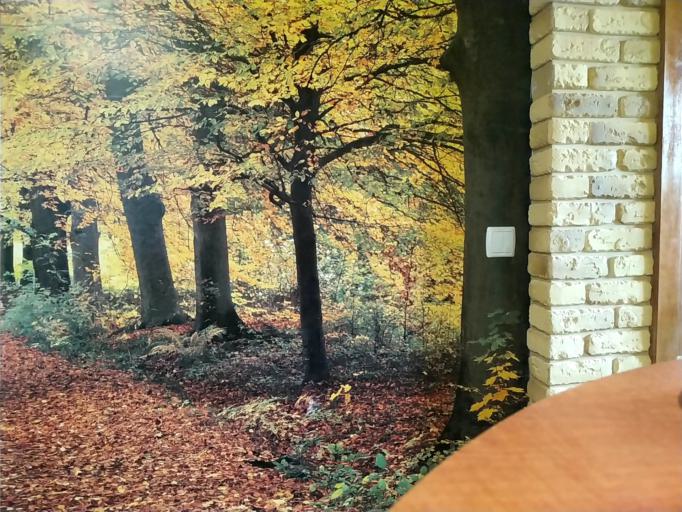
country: RU
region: Novgorod
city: Opechenskiy Posad
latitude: 58.2673
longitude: 34.0255
